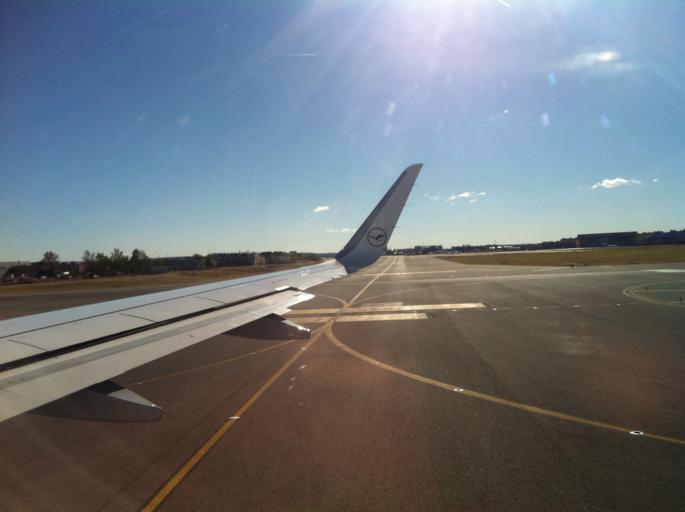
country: ES
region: Madrid
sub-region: Provincia de Madrid
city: Barajas de Madrid
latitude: 40.4886
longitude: -3.5701
